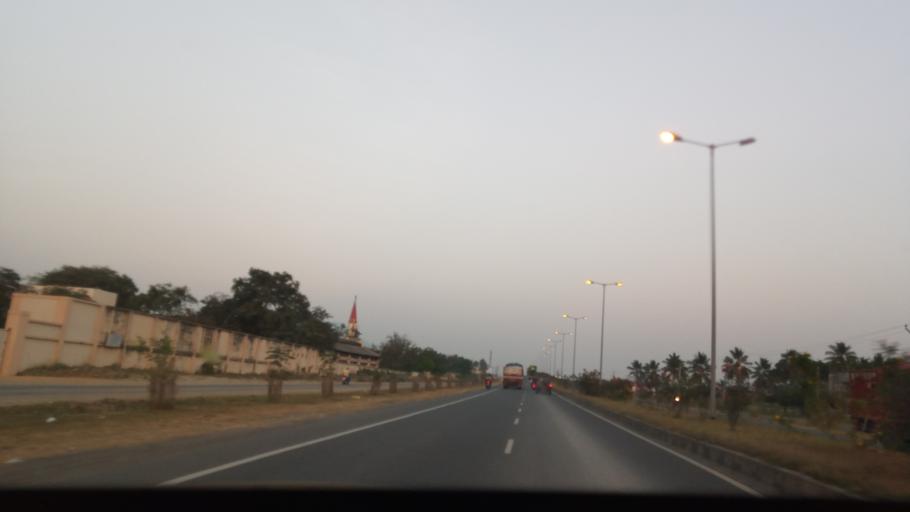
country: IN
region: Tamil Nadu
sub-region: Salem
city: Salem
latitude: 11.6654
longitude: 78.2764
